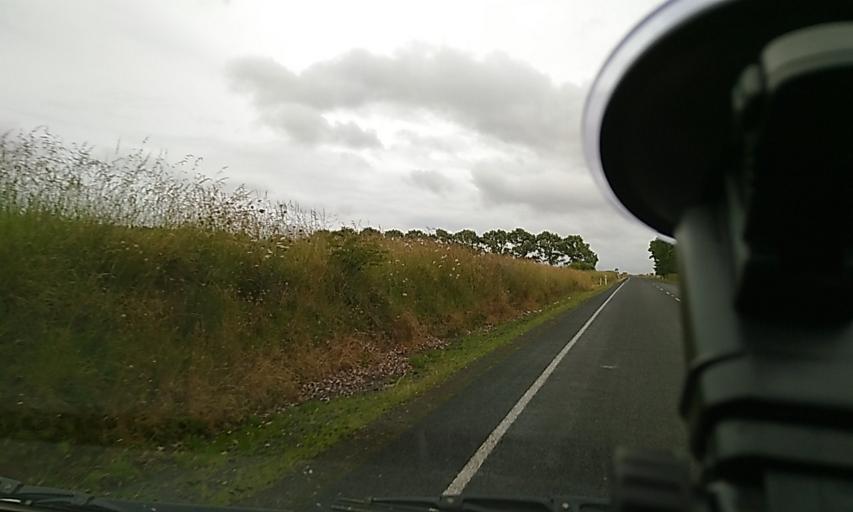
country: NZ
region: Auckland
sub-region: Auckland
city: Pukekohe East
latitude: -37.3183
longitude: 174.9631
